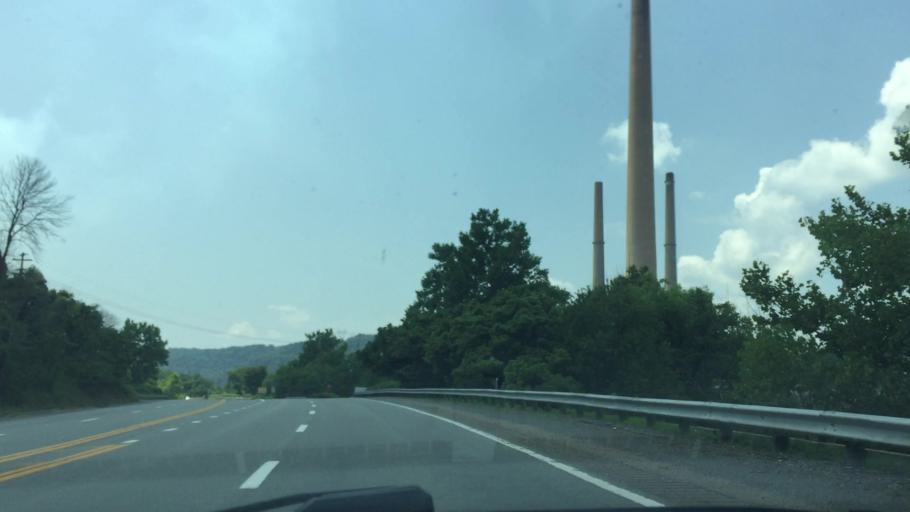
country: US
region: Ohio
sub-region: Belmont County
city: Powhatan Point
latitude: 39.8493
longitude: -80.8133
